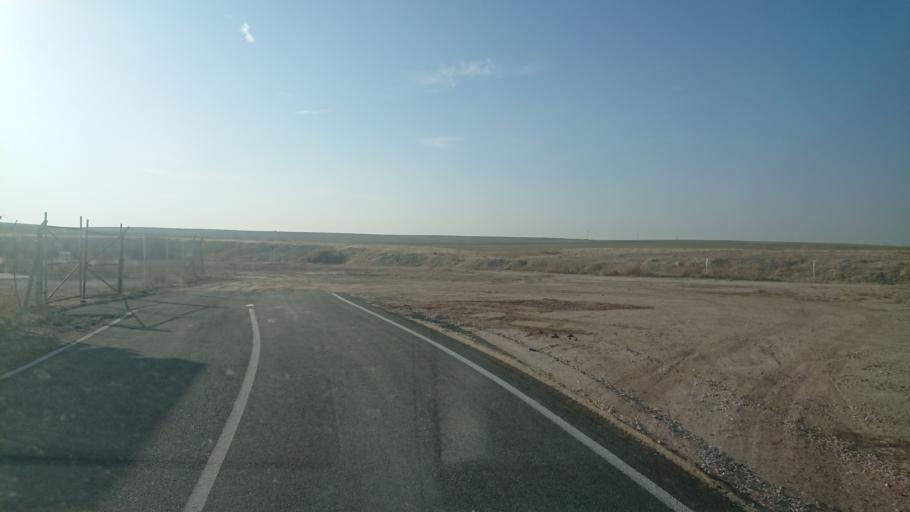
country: TR
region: Aksaray
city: Sultanhani
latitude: 38.0843
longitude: 33.6111
